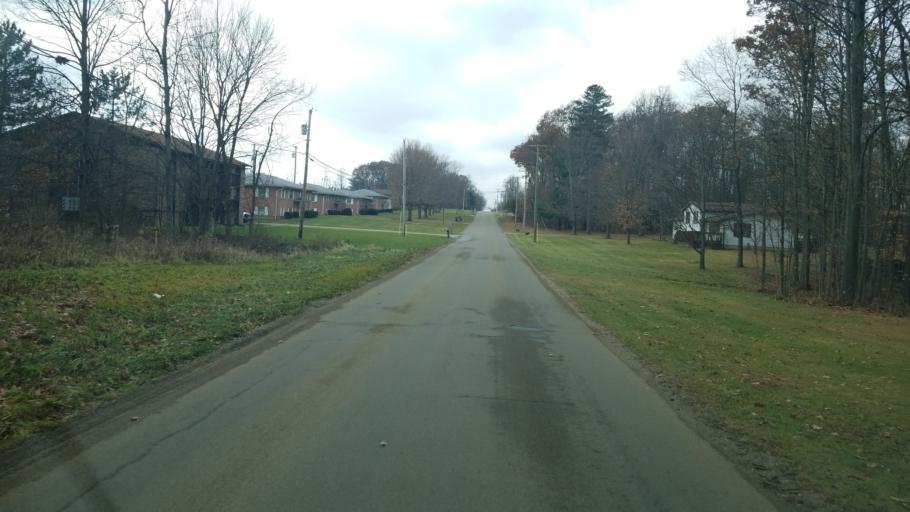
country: US
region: Ohio
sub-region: Richland County
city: Lincoln Heights
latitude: 40.7997
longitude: -82.4768
